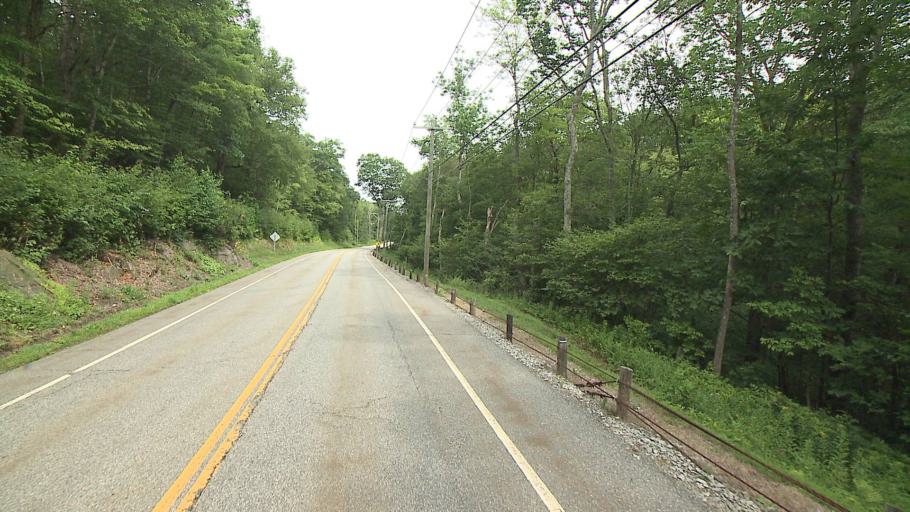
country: US
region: Connecticut
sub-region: Litchfield County
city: New Preston
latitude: 41.7382
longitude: -73.3396
